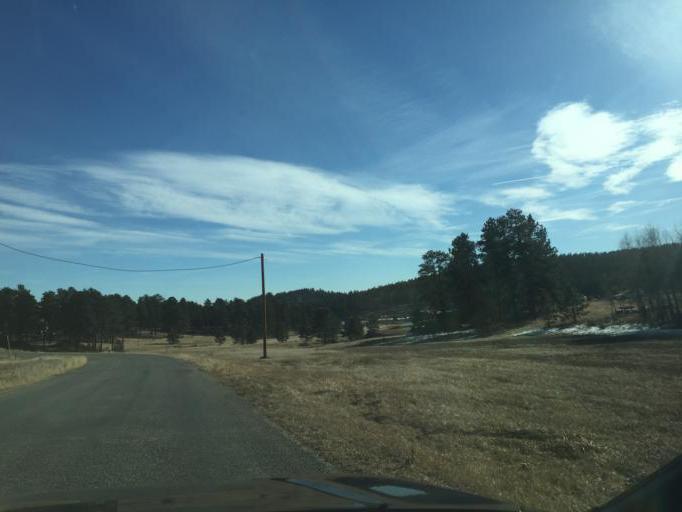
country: US
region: Colorado
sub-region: Jefferson County
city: Evergreen
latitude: 39.4426
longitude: -105.4583
